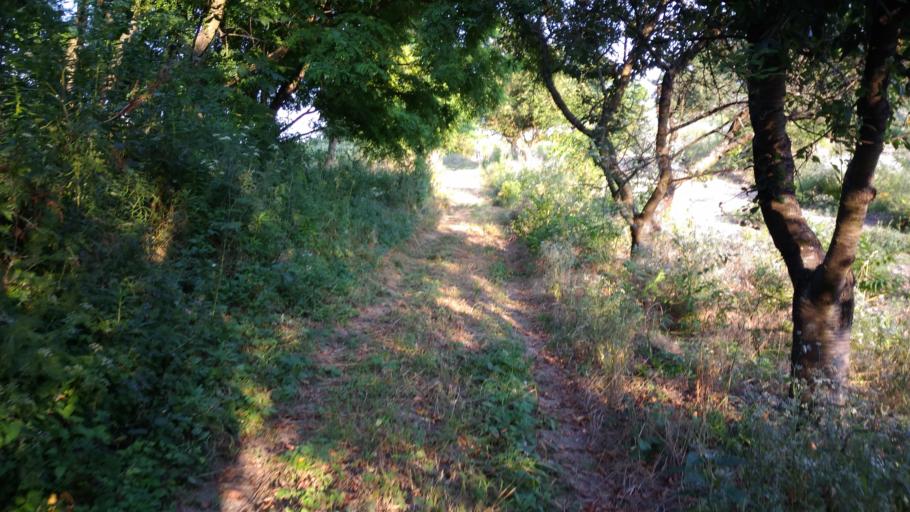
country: HU
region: Fejer
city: Bicske
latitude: 47.4664
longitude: 18.6888
